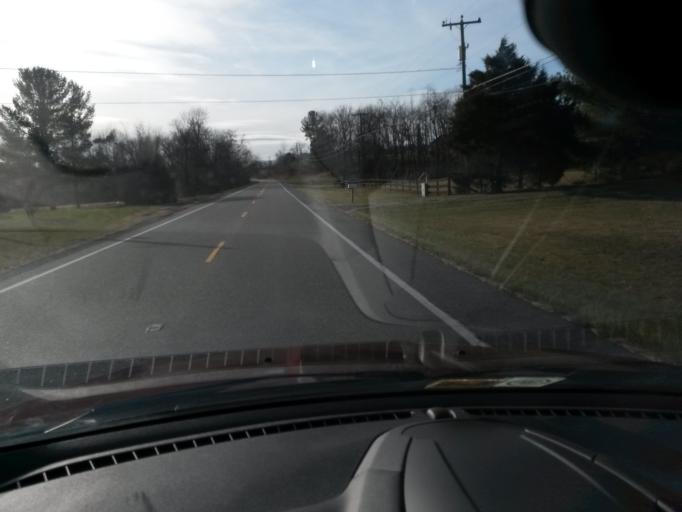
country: US
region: Virginia
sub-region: Augusta County
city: Jolivue
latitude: 38.0958
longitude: -79.3364
